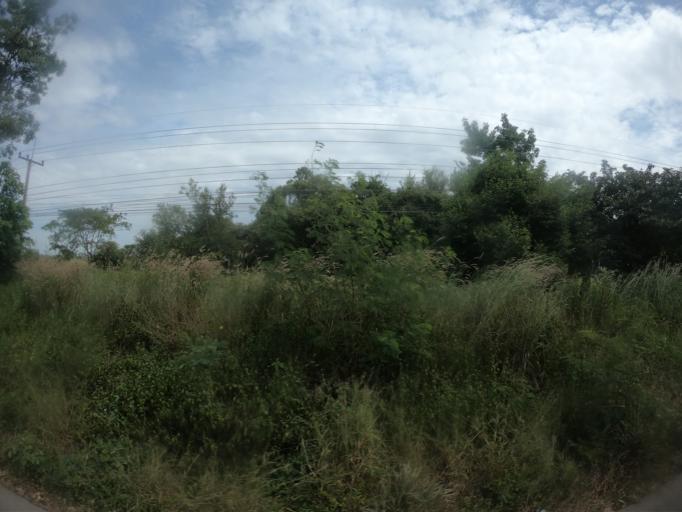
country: TH
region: Maha Sarakham
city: Chiang Yuen
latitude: 16.3543
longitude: 103.1164
